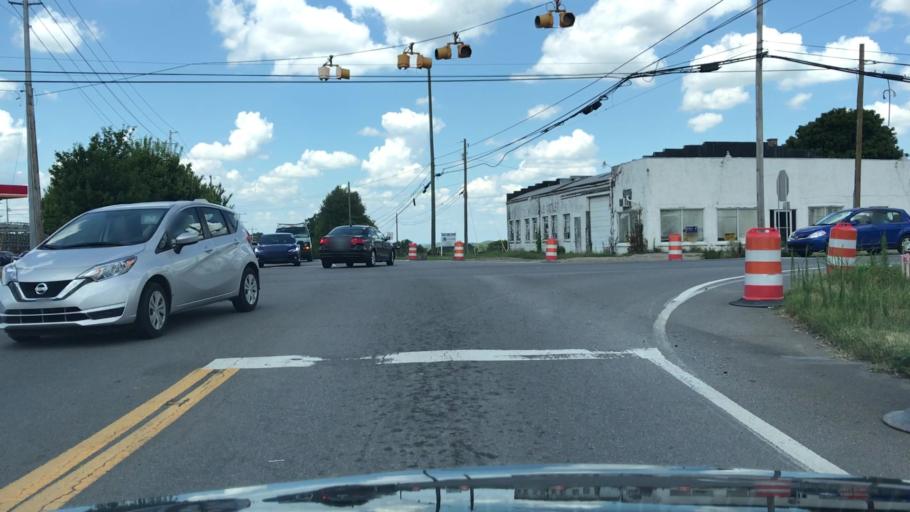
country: US
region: Tennessee
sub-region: Williamson County
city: Nolensville
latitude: 35.8543
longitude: -86.6586
